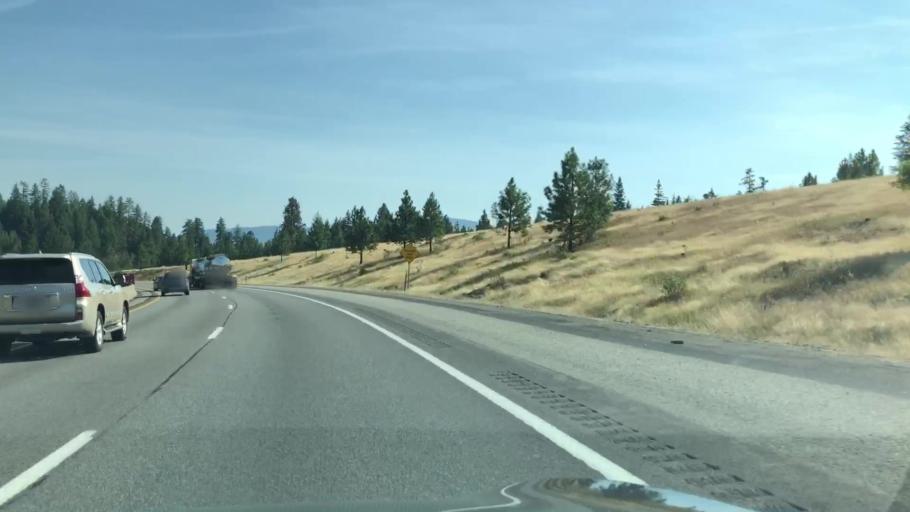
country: US
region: Idaho
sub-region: Kootenai County
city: Coeur d'Alene
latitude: 47.6550
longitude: -116.7271
